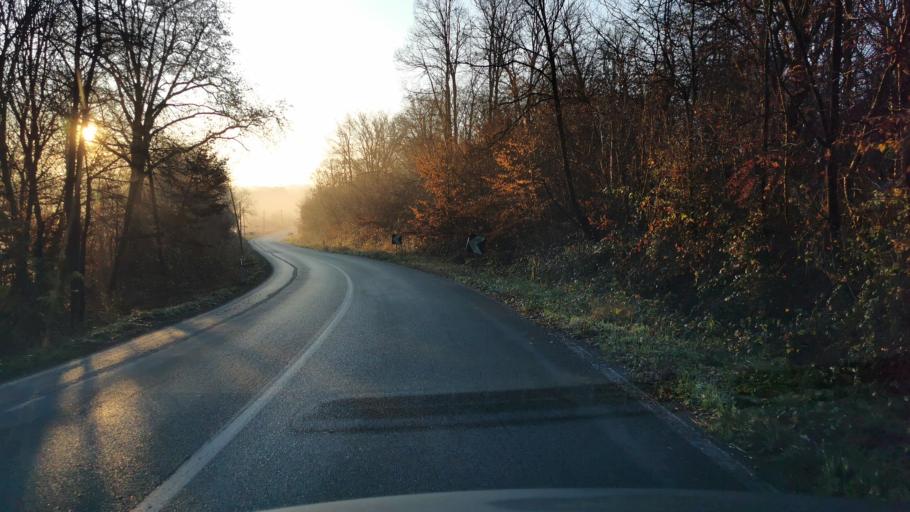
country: IT
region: Piedmont
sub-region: Provincia di Torino
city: La Cassa
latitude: 45.1629
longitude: 7.5284
